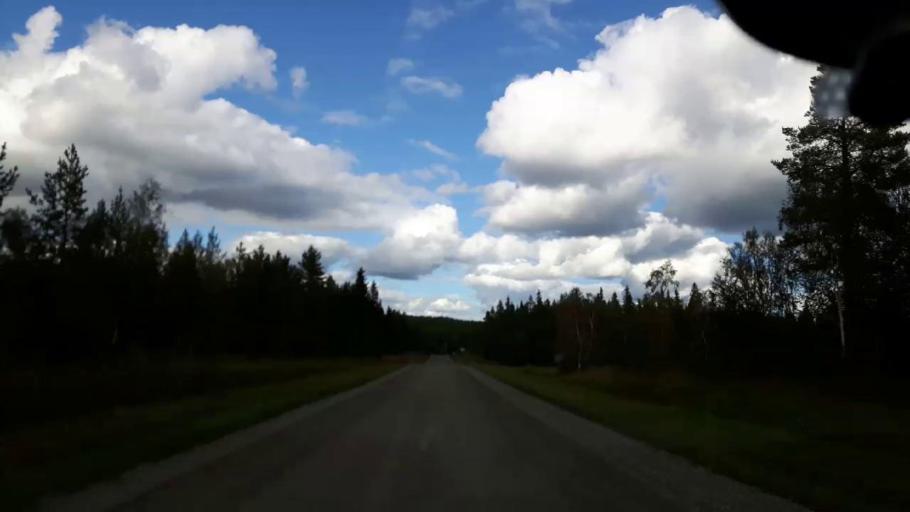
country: SE
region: Jaemtland
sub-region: Stroemsunds Kommun
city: Stroemsund
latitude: 63.4112
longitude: 15.5633
